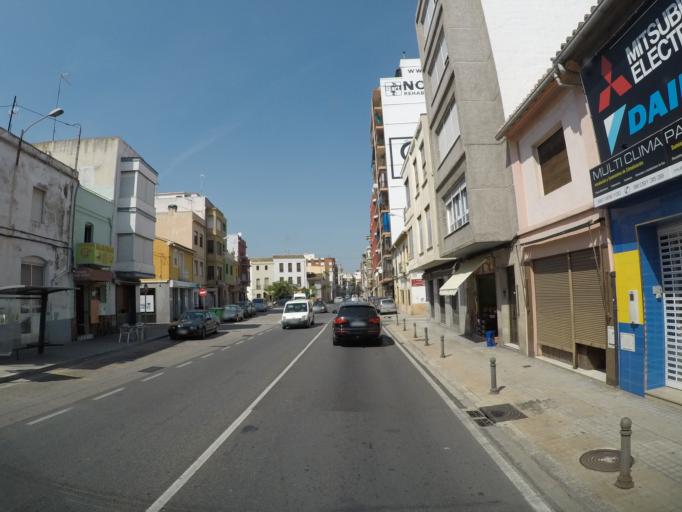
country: ES
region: Valencia
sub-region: Provincia de Valencia
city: Oliva
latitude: 38.9162
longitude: -0.1156
